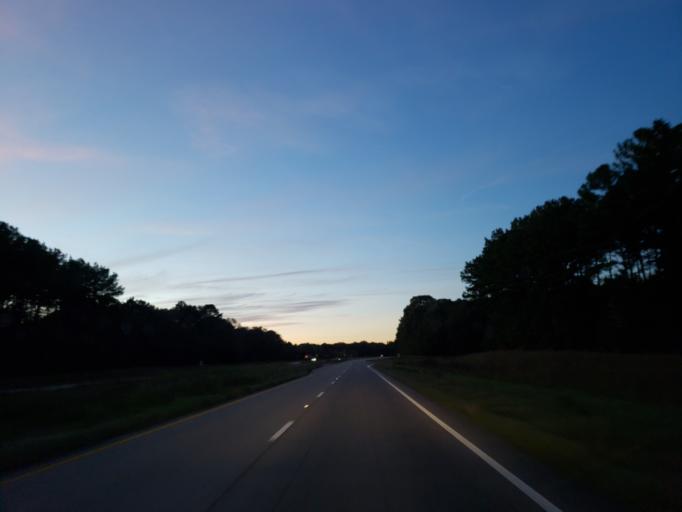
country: US
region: Mississippi
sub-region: Wayne County
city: Waynesboro
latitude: 31.8458
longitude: -88.7126
